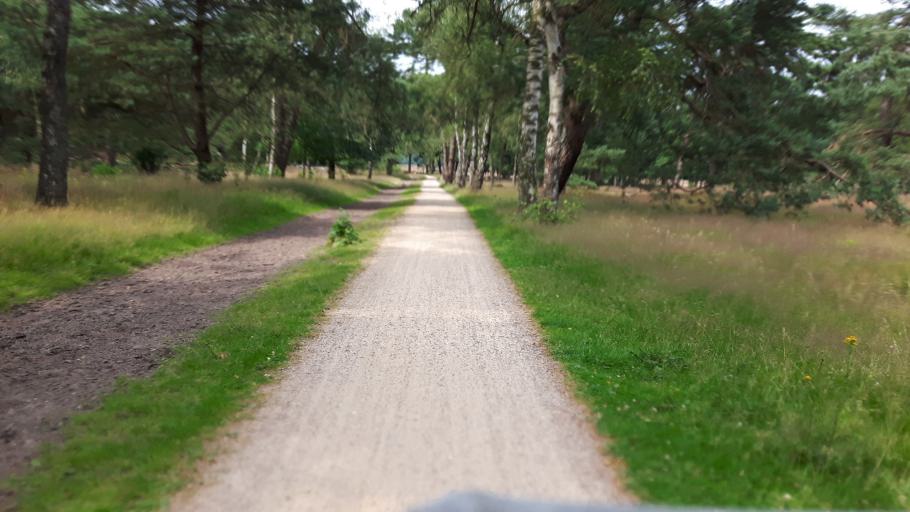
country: NL
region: North Holland
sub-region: Gemeente Hilversum
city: Hilversum
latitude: 52.1955
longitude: 5.1692
